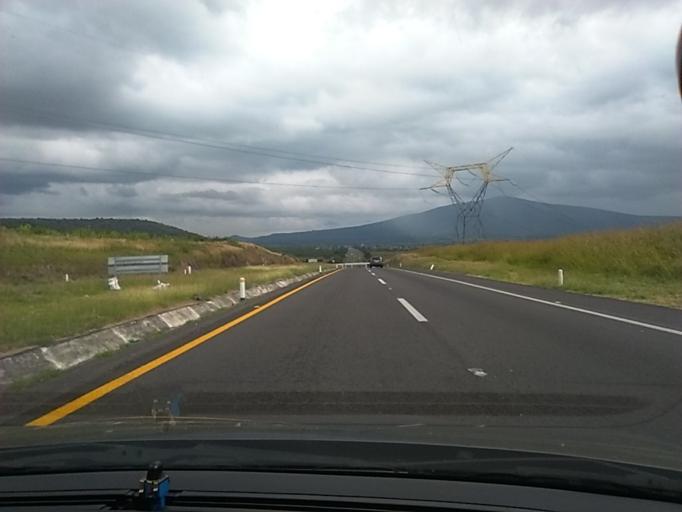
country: MX
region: Jalisco
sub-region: Zapotlanejo
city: La Mezquitera
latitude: 20.5829
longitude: -103.0958
